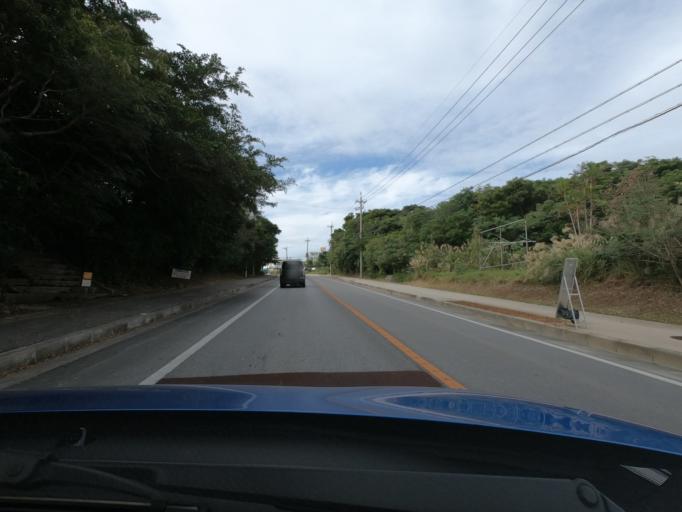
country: JP
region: Okinawa
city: Nago
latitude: 26.6799
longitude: 127.8870
